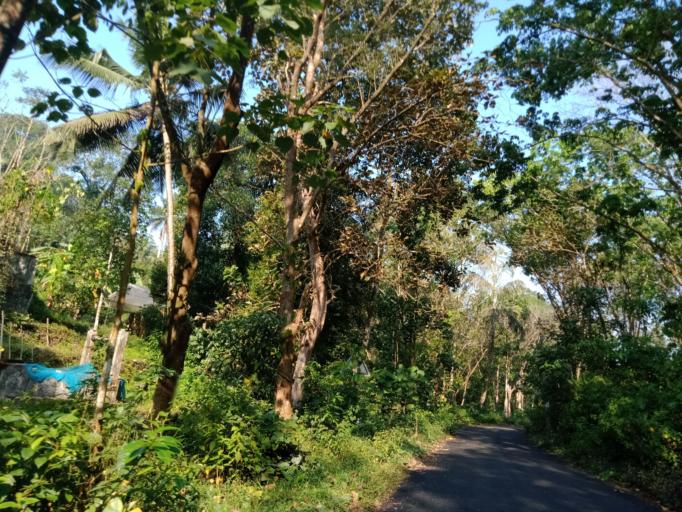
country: IN
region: Kerala
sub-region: Kottayam
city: Lalam
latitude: 9.5987
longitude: 76.7023
